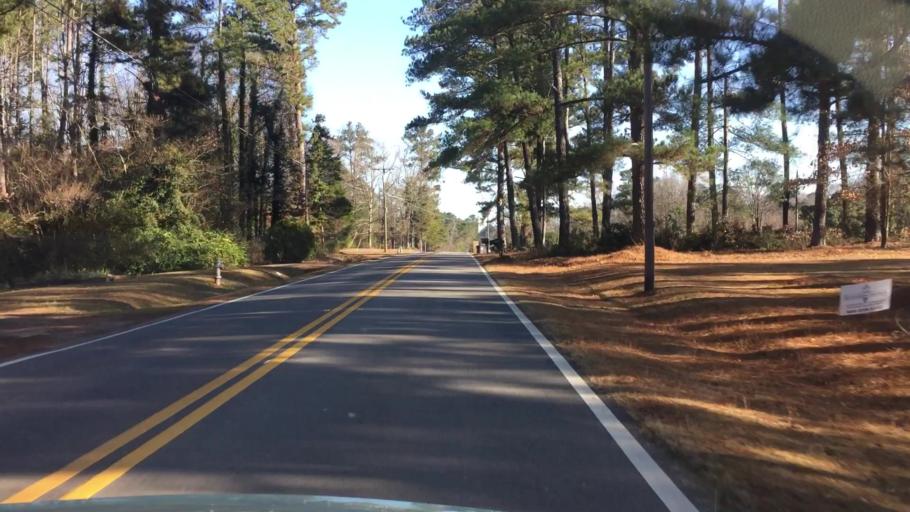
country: US
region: Georgia
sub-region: Henry County
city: McDonough
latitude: 33.5140
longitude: -84.1360
